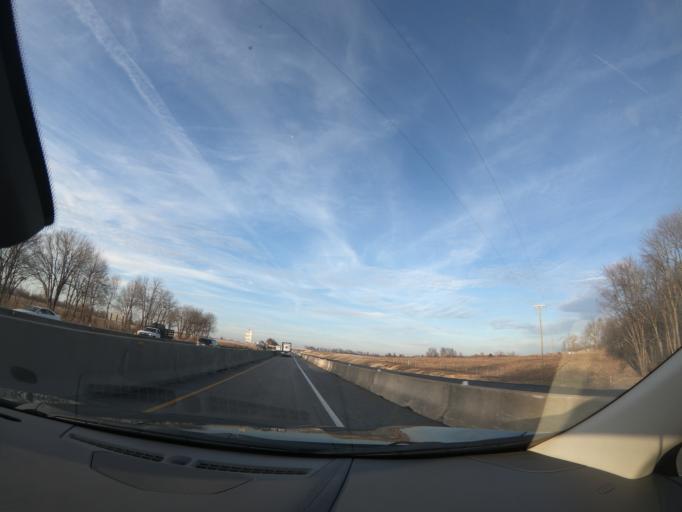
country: US
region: Kentucky
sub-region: Hardin County
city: Elizabethtown
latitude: 37.5680
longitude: -85.8748
